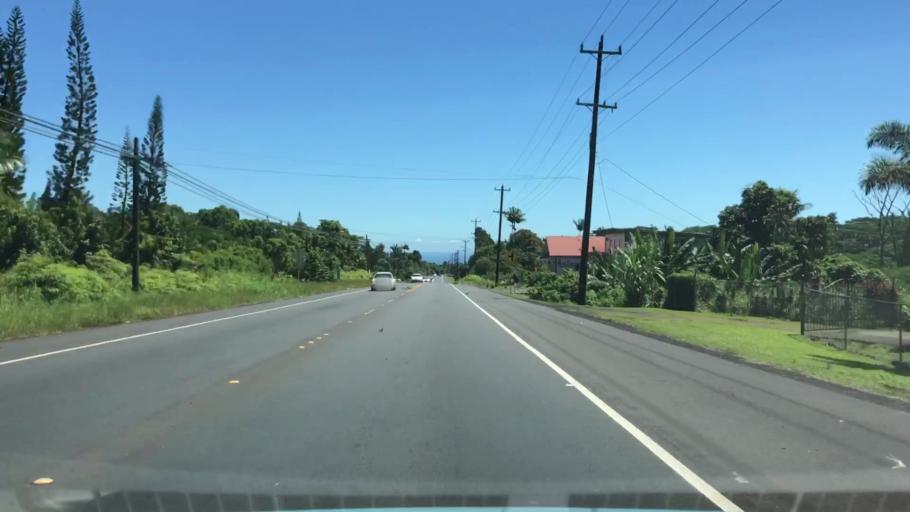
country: US
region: Hawaii
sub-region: Hawaii County
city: Mountain View
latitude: 19.5662
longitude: -155.0859
